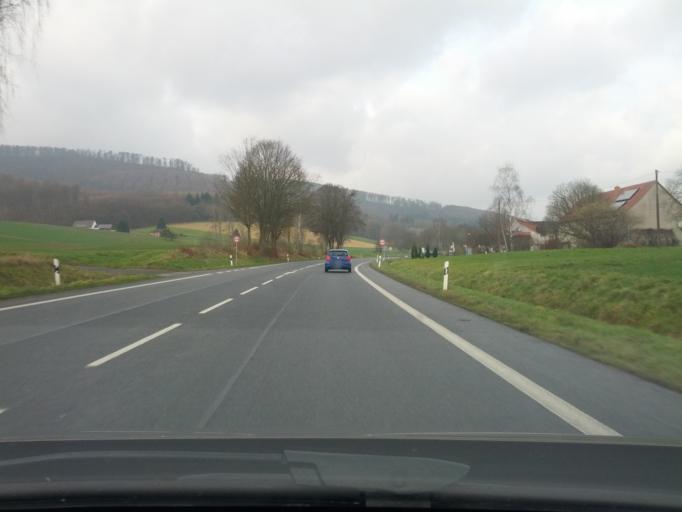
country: DE
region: Lower Saxony
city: Bodenfelde
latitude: 51.5641
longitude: 9.5945
